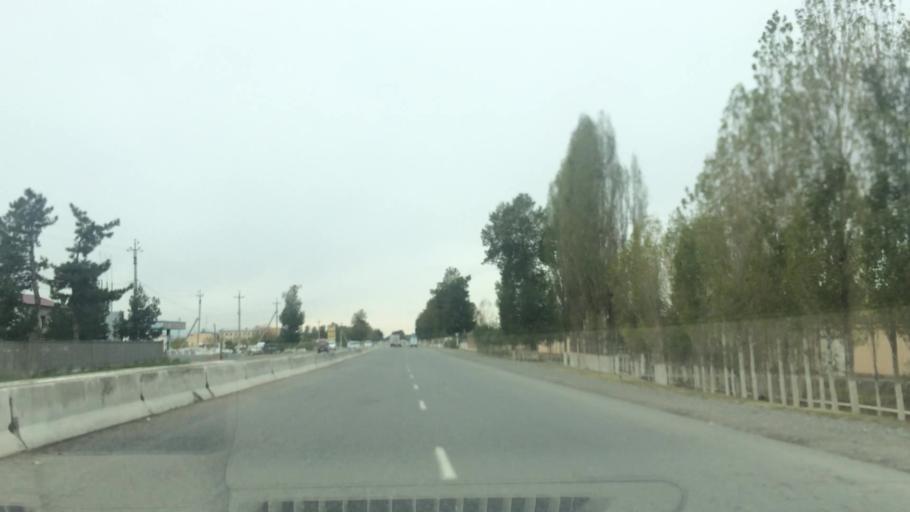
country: UZ
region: Samarqand
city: Jomboy
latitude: 39.7225
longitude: 67.1272
